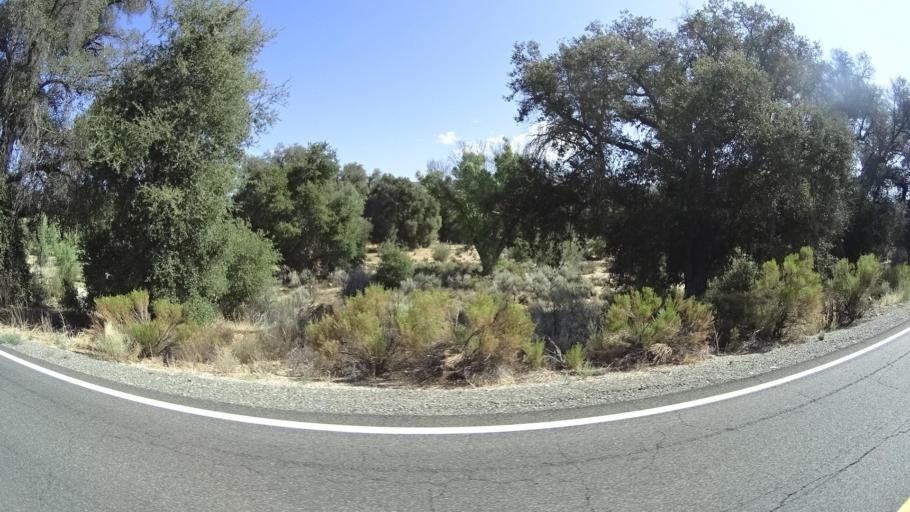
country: US
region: California
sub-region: Riverside County
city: Aguanga
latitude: 33.3329
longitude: -116.7119
